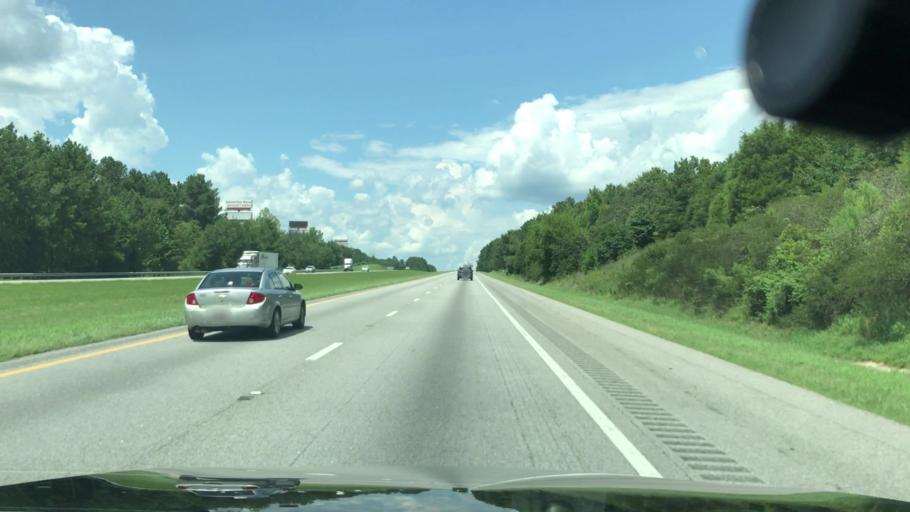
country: US
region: South Carolina
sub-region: Chester County
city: Great Falls
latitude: 34.5908
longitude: -81.0153
